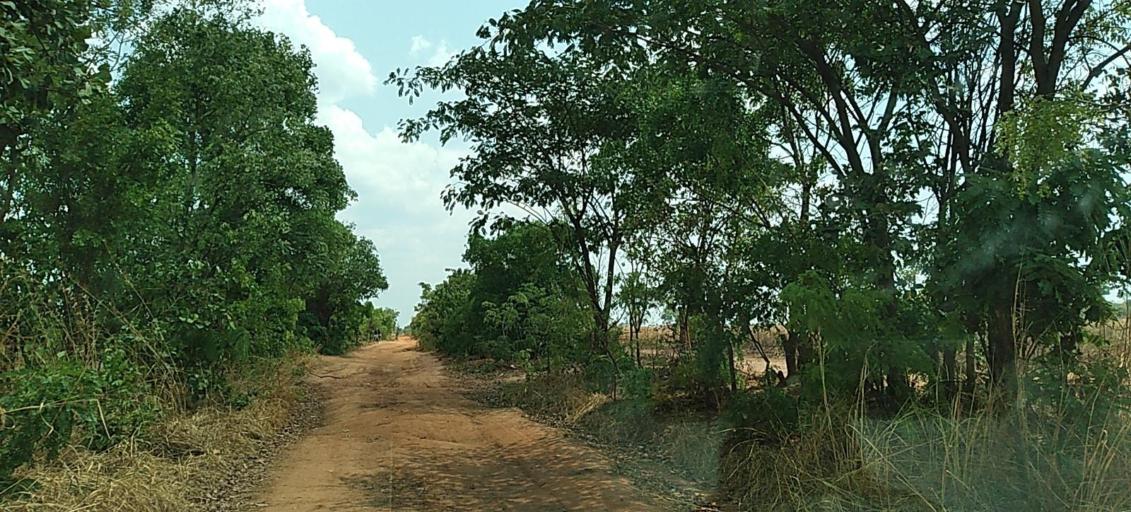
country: ZM
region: Copperbelt
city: Mpongwe
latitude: -13.6582
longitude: 28.0250
